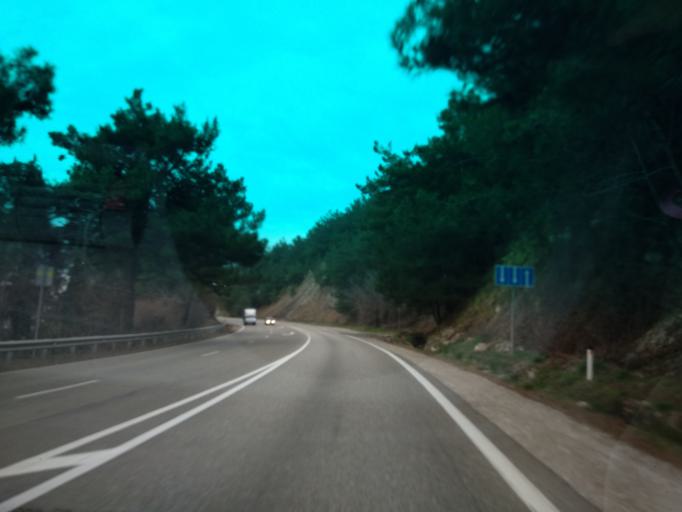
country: RU
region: Krasnodarskiy
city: Ol'ginka
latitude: 44.1876
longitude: 38.9092
